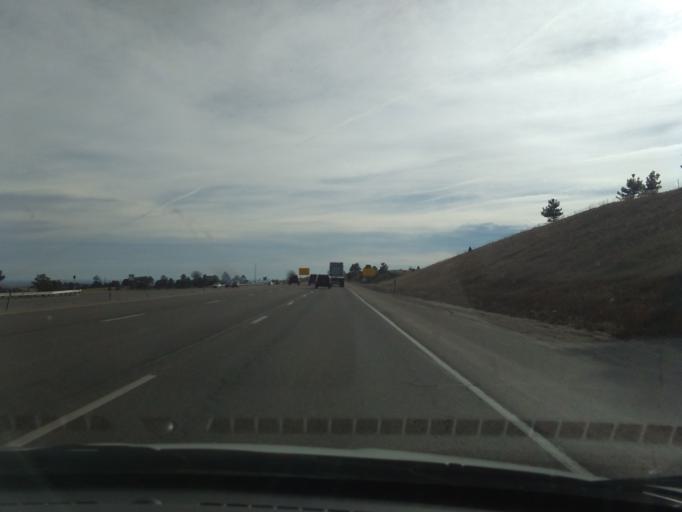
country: US
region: Colorado
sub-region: Jefferson County
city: Genesee
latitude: 39.7078
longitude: -105.2809
